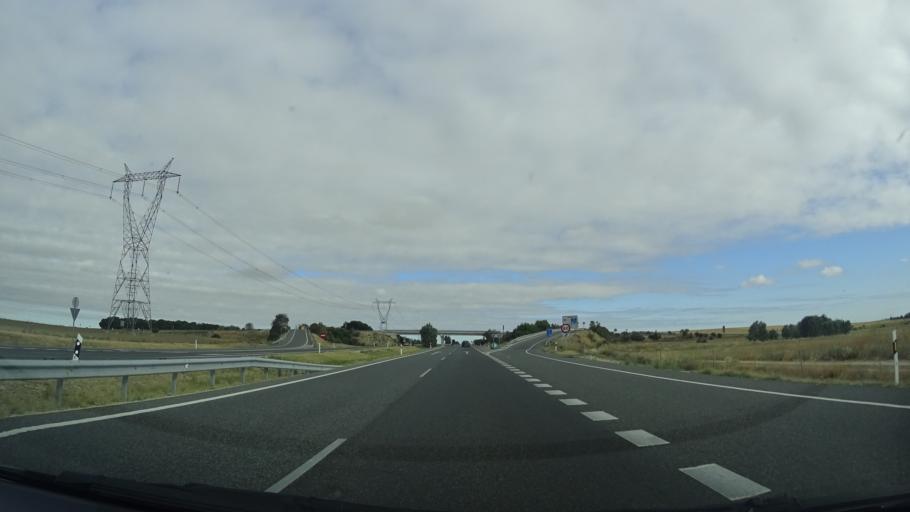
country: ES
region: Castille and Leon
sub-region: Provincia de Valladolid
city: San Pablo de la Moraleja
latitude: 41.1472
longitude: -4.7873
